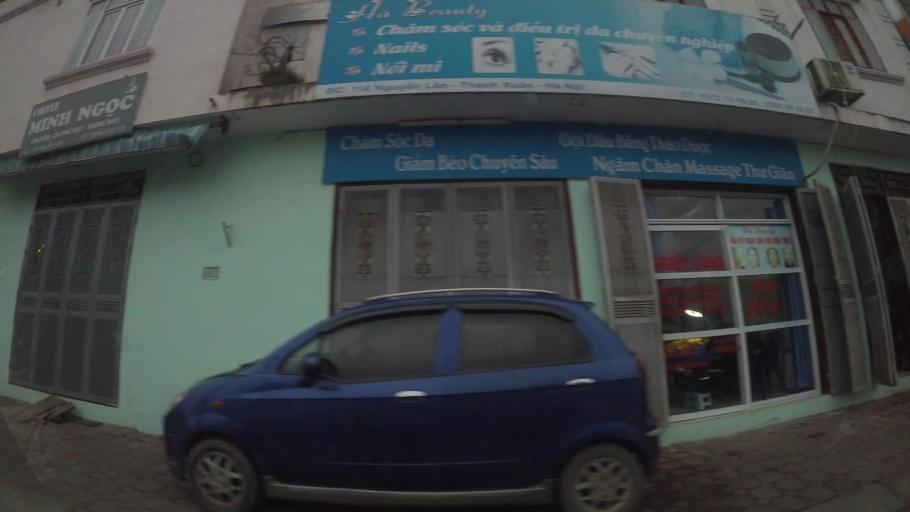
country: VN
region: Ha Noi
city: Hai BaTrung
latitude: 20.9912
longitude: 105.8368
